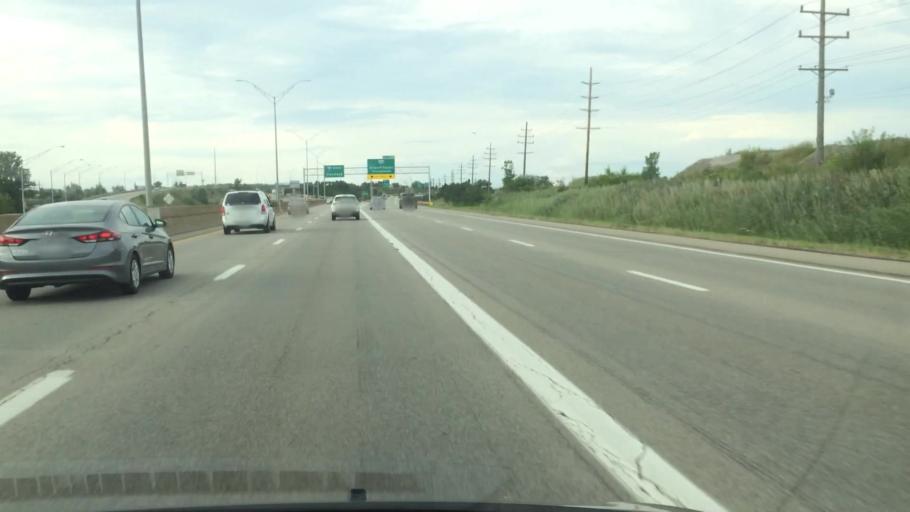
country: US
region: Ohio
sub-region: Cuyahoga County
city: Brook Park
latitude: 41.4133
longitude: -81.8177
